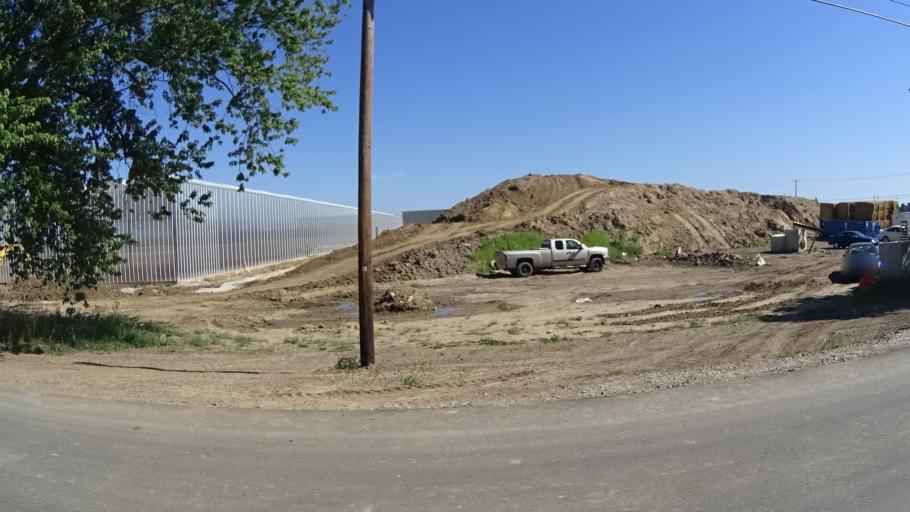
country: US
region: Ohio
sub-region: Erie County
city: Huron
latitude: 41.3892
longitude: -82.5918
